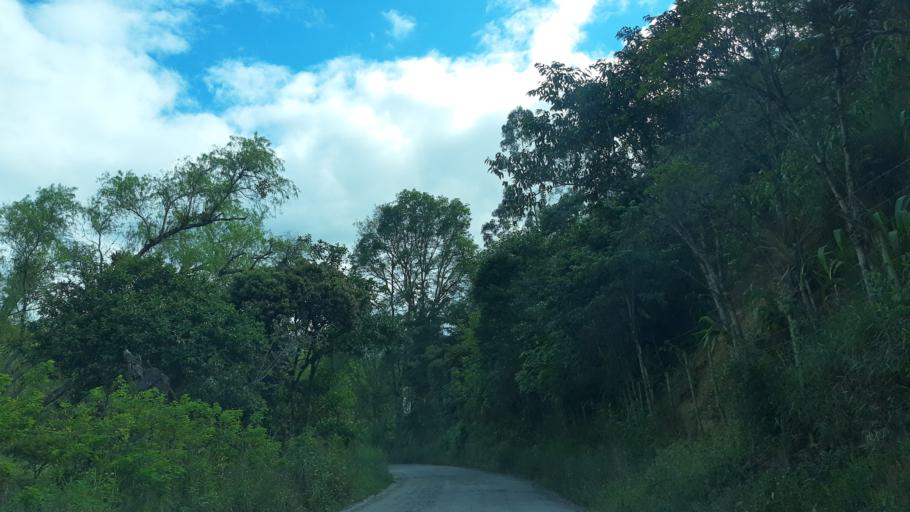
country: CO
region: Cundinamarca
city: Tenza
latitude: 5.0580
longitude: -73.4177
